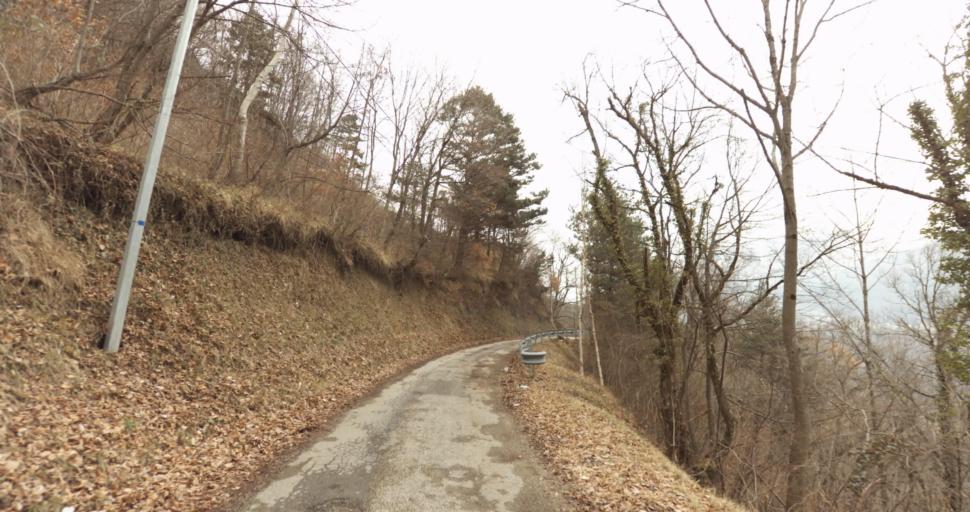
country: FR
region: Rhone-Alpes
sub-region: Departement de l'Isere
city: Saint-Georges-de-Commiers
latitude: 45.0152
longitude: 5.6833
